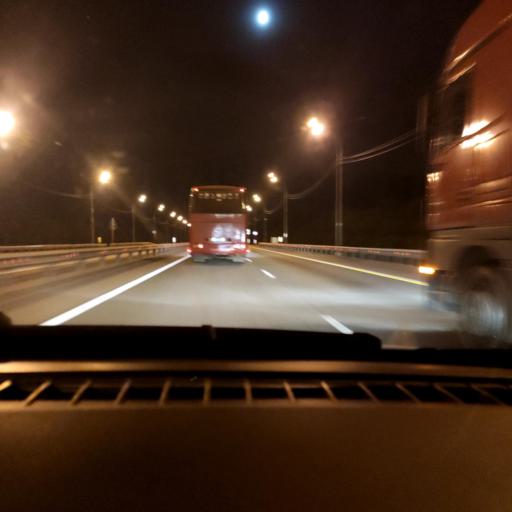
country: RU
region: Lipetsk
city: Khlevnoye
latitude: 52.2353
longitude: 39.0801
